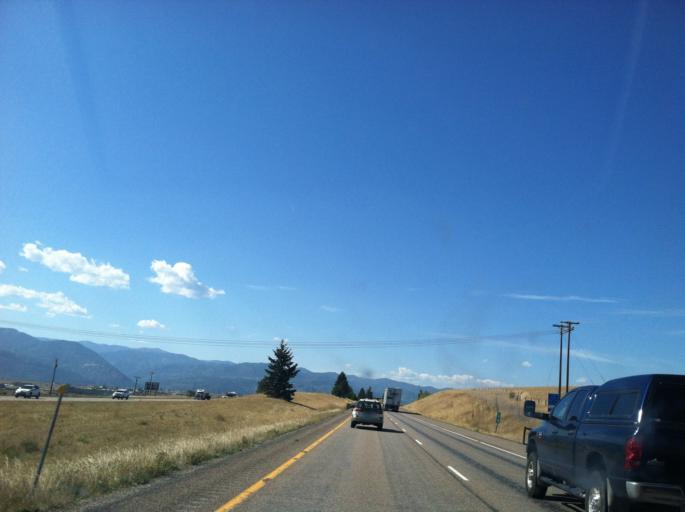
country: US
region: Montana
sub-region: Missoula County
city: Orchard Homes
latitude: 46.9383
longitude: -114.1013
